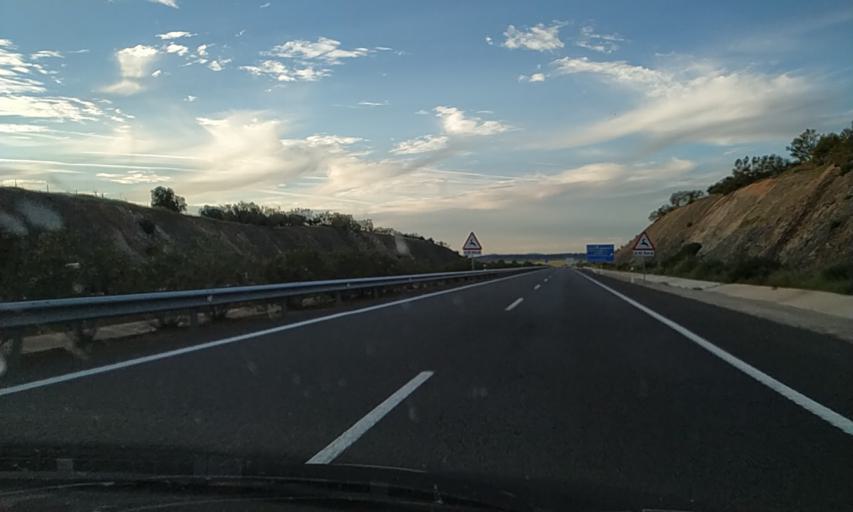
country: ES
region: Extremadura
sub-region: Provincia de Badajoz
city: Aljucen
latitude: 39.0285
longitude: -6.3342
